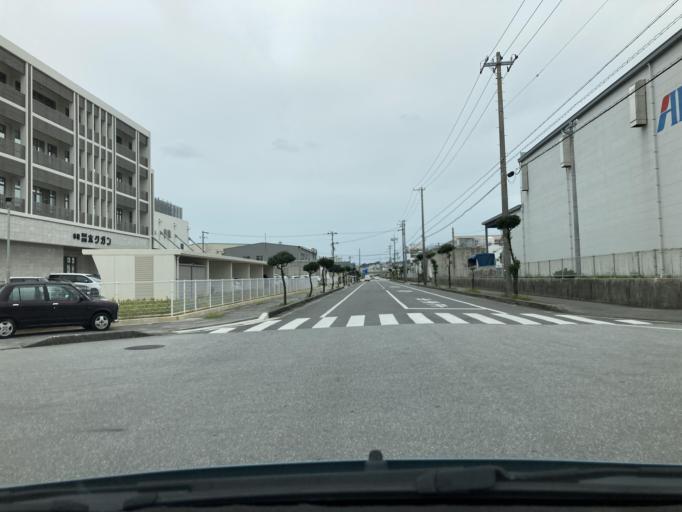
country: JP
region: Okinawa
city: Itoman
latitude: 26.1378
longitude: 127.6542
